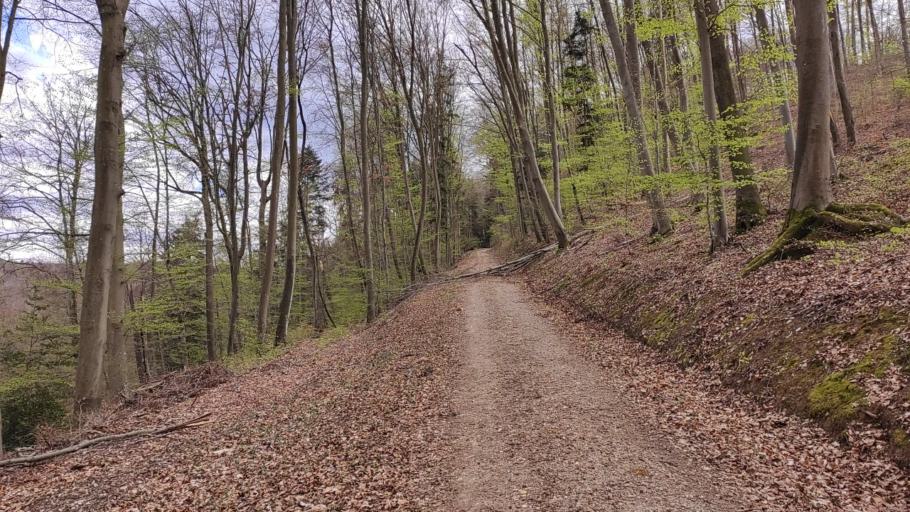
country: DE
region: Baden-Wuerttemberg
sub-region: Freiburg Region
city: Ebringen
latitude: 47.9474
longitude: 7.7765
